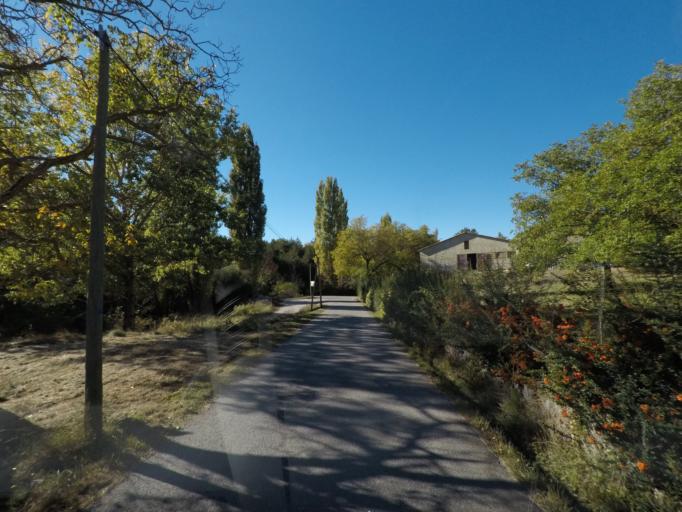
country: FR
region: Provence-Alpes-Cote d'Azur
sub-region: Departement des Hautes-Alpes
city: Serres
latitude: 44.4446
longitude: 5.5525
